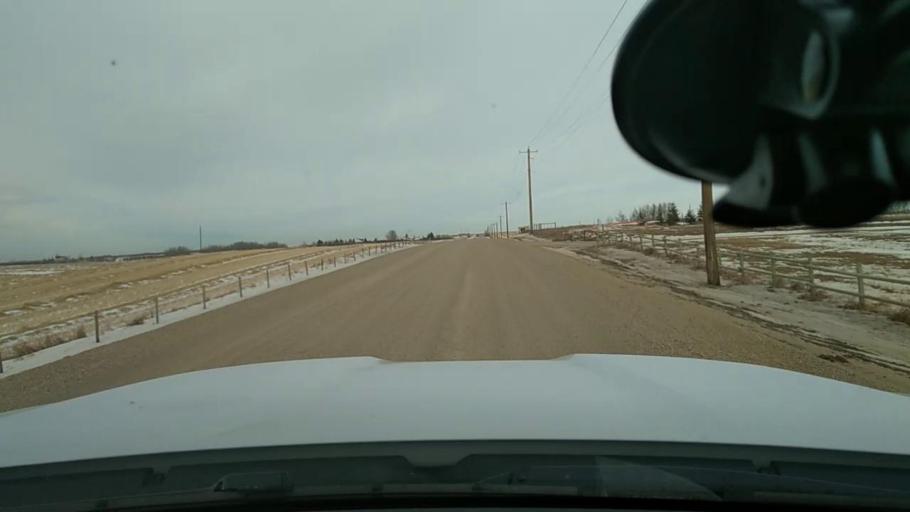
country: CA
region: Alberta
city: Airdrie
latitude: 51.2253
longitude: -113.9118
